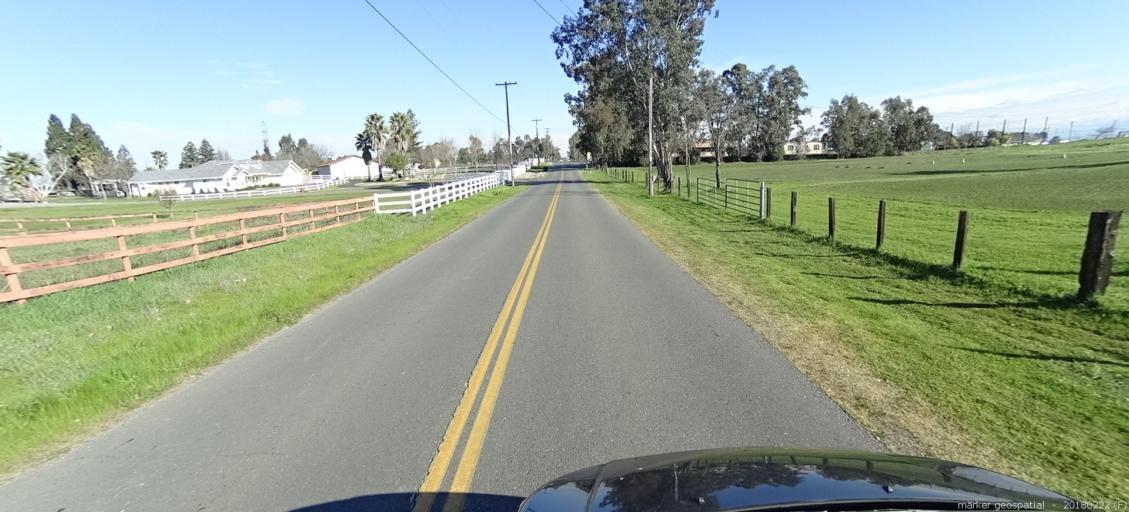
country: US
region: California
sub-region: Sacramento County
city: Elverta
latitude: 38.7298
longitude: -121.4669
